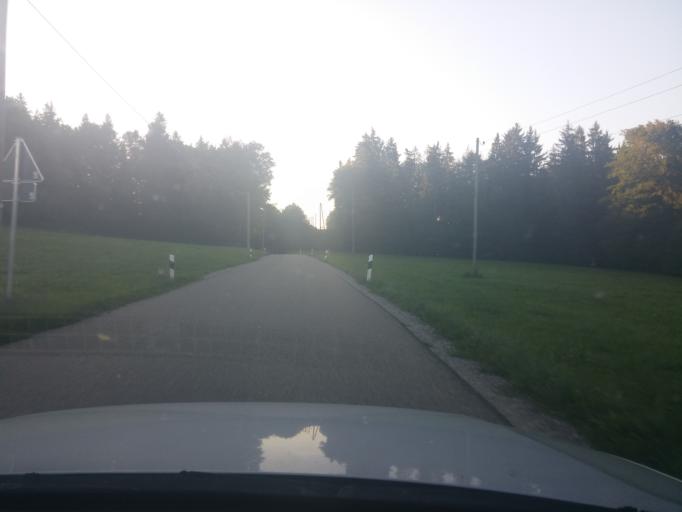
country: DE
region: Bavaria
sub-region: Swabia
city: Altusried
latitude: 47.8244
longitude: 10.1775
